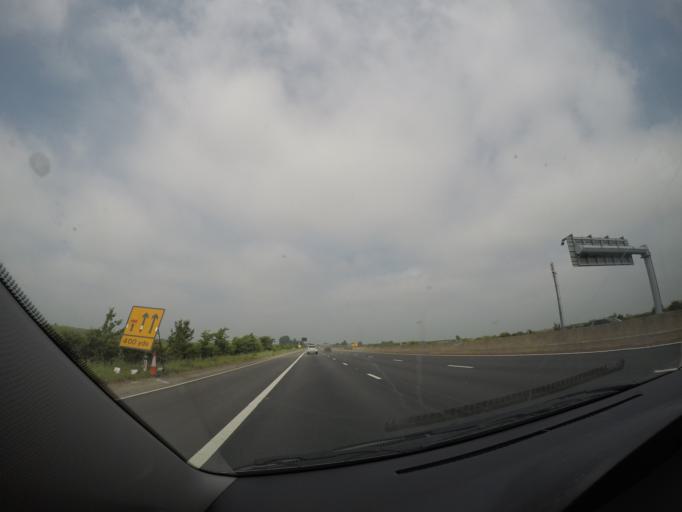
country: GB
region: England
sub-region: North Yorkshire
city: Boroughbridge
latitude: 54.1556
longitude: -1.4416
